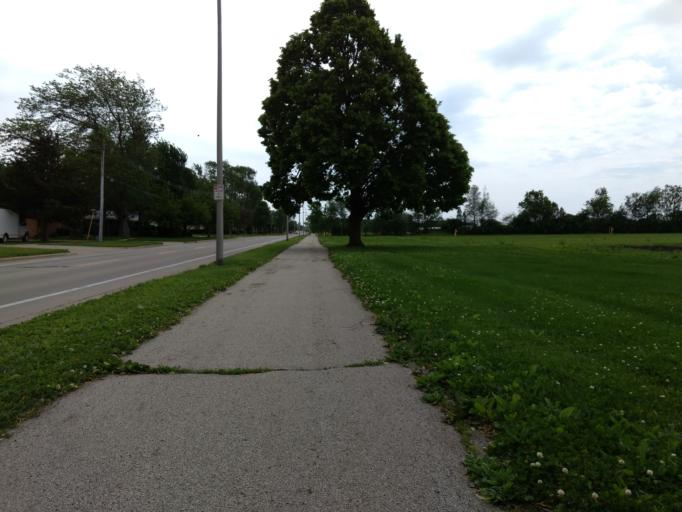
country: US
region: Illinois
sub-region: Champaign County
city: Urbana
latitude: 40.0885
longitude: -88.2096
